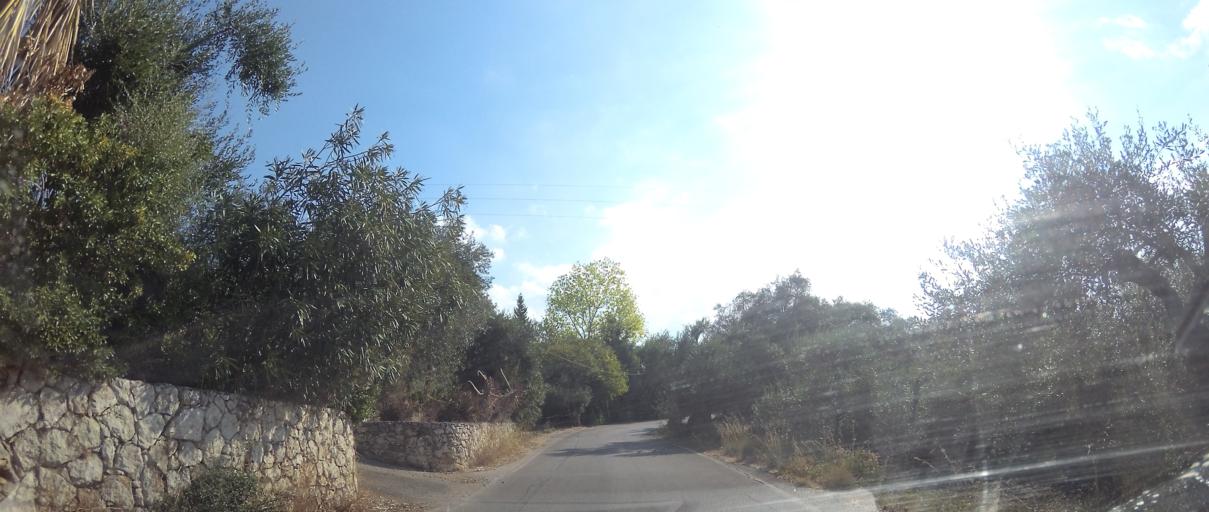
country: GR
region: Ionian Islands
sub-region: Nomos Kerkyras
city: Kontokali
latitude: 39.7119
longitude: 19.8461
